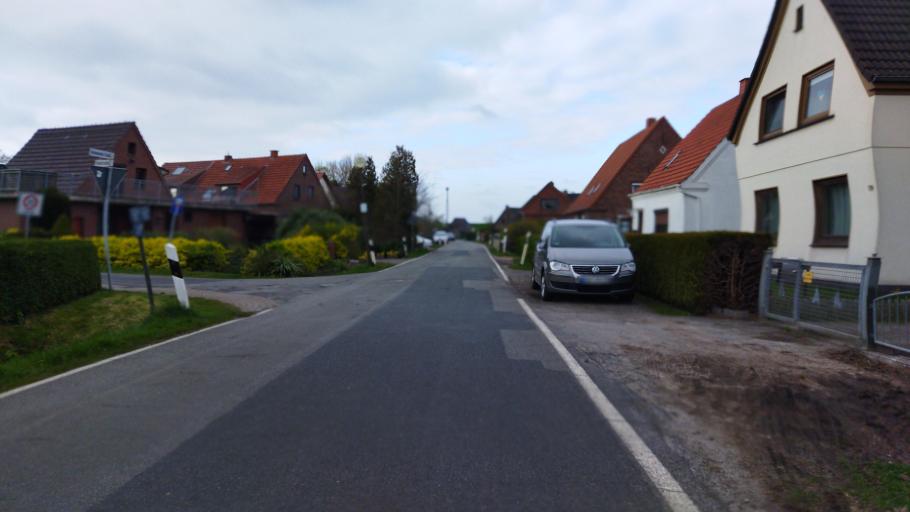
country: DE
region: Lower Saxony
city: Lemwerder
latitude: 53.1646
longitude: 8.5821
